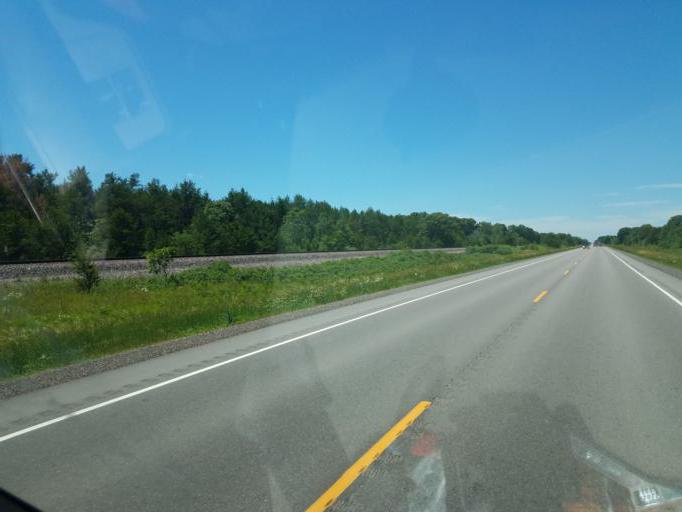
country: US
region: Wisconsin
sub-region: Juneau County
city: New Lisbon
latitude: 44.0247
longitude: -90.1245
